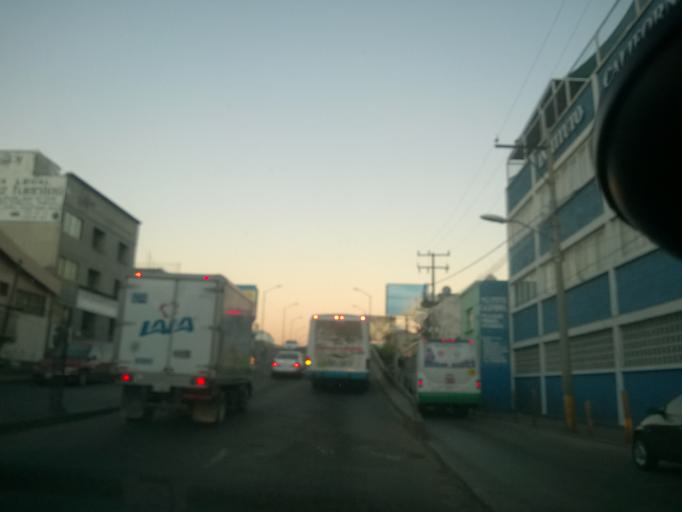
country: MX
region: Guanajuato
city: Leon
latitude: 21.1157
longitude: -101.6860
